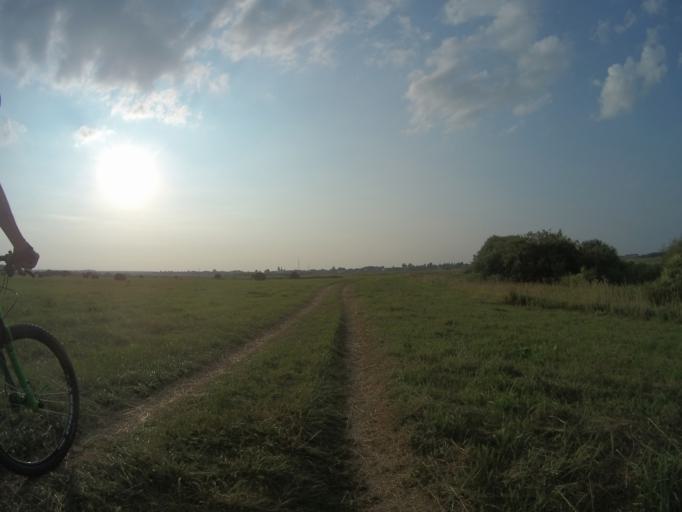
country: RU
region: Vladimir
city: Orgtrud
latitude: 56.3000
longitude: 40.6249
